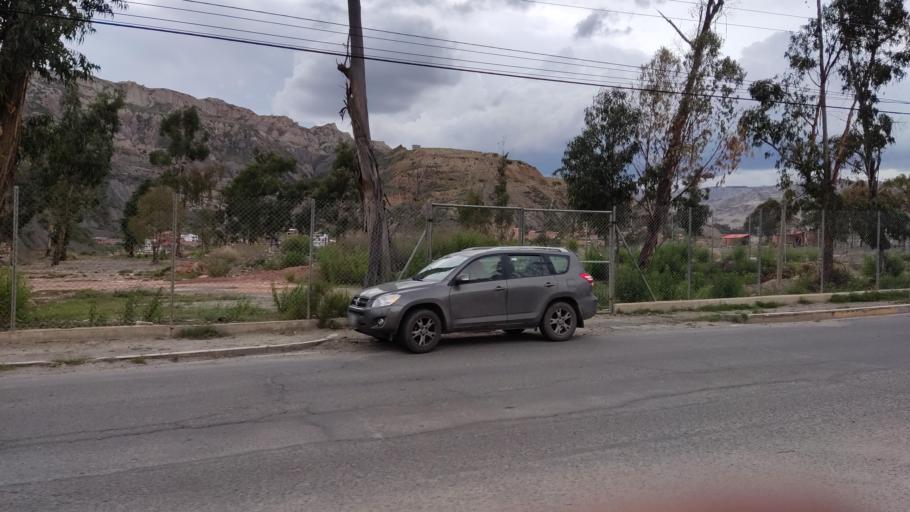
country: BO
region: La Paz
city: La Paz
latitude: -16.5800
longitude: -68.0801
